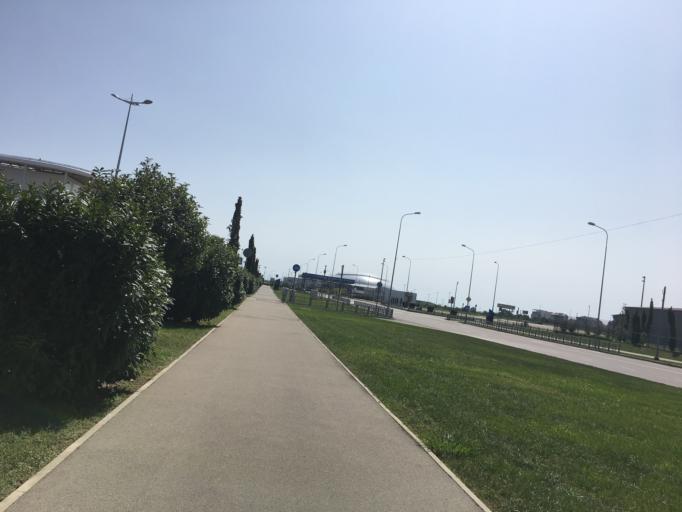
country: RU
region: Krasnodarskiy
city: Adler
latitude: 43.4148
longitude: 39.9480
